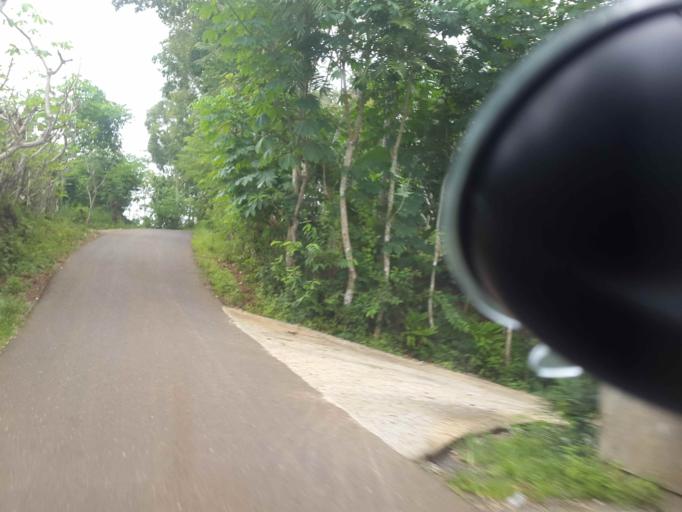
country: ID
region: Central Java
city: Binangun
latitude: -7.5398
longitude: 109.2469
